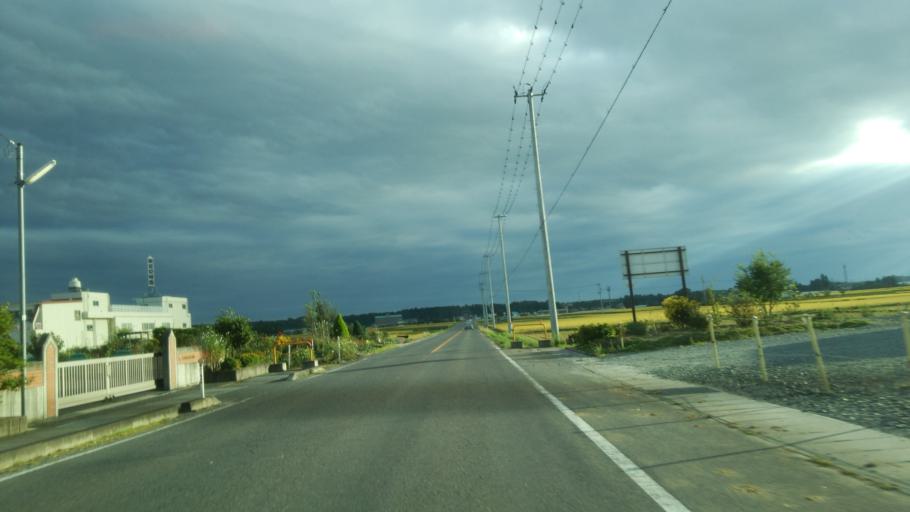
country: JP
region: Fukushima
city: Koriyama
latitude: 37.3738
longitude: 140.3410
